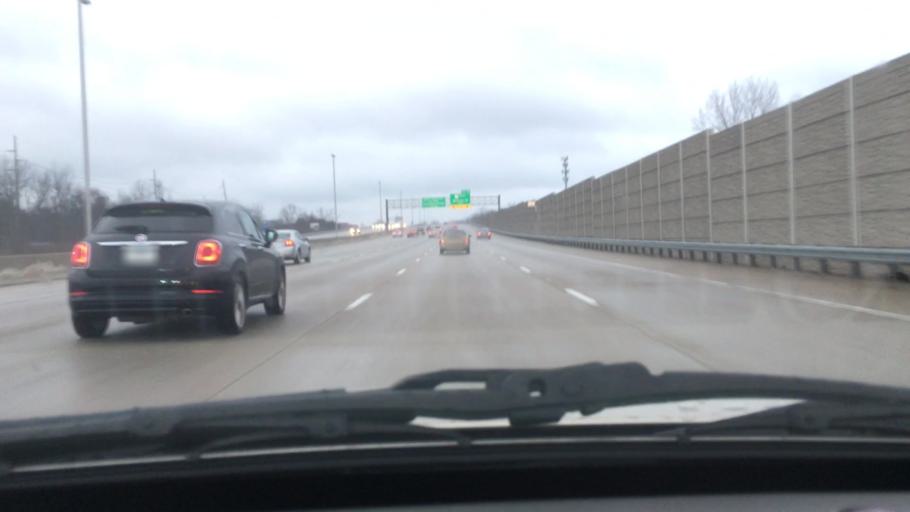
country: US
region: Indiana
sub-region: Marion County
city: Meridian Hills
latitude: 39.9267
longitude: -86.1299
